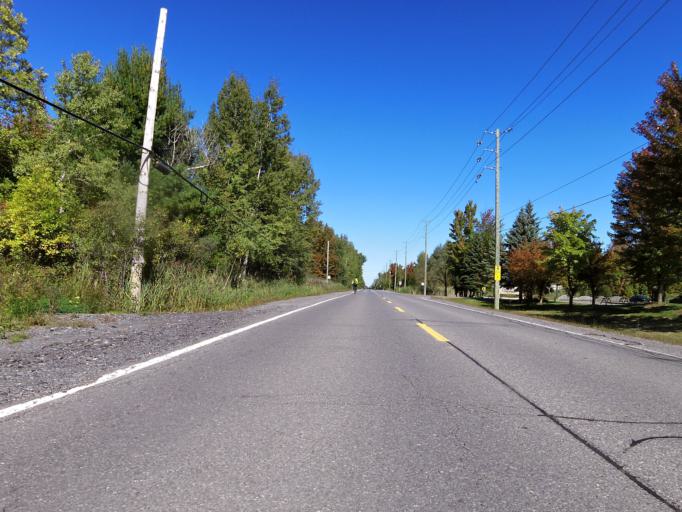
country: CA
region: Ontario
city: Clarence-Rockland
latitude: 45.3554
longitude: -75.4488
